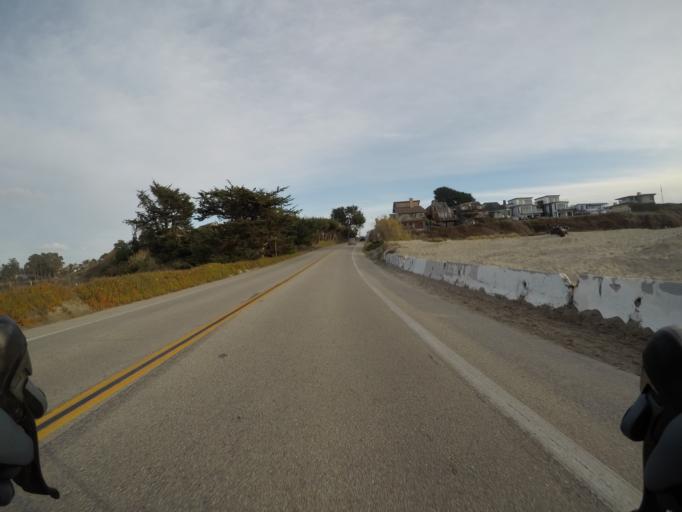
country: US
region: California
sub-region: Santa Cruz County
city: Twin Lakes
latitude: 36.9605
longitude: -121.9836
